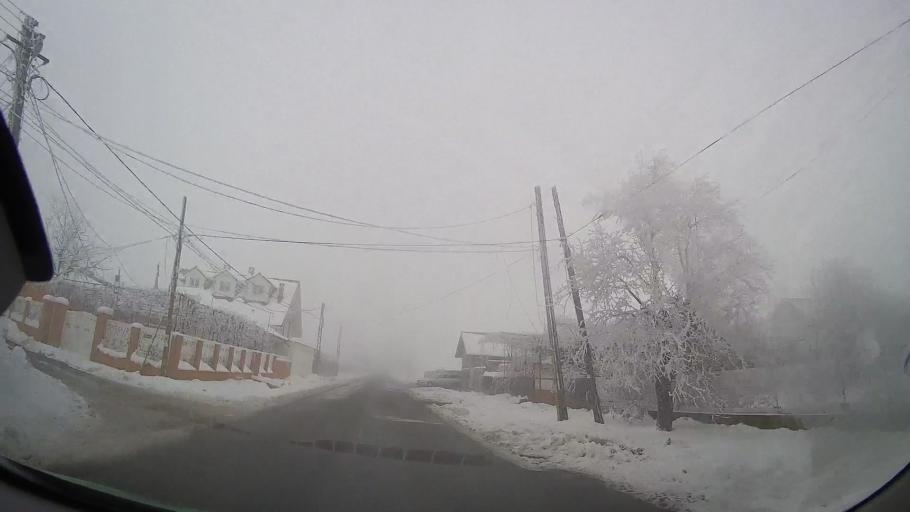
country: RO
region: Neamt
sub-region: Comuna Sabaoani
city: Sabaoani
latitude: 47.0257
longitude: 26.8616
